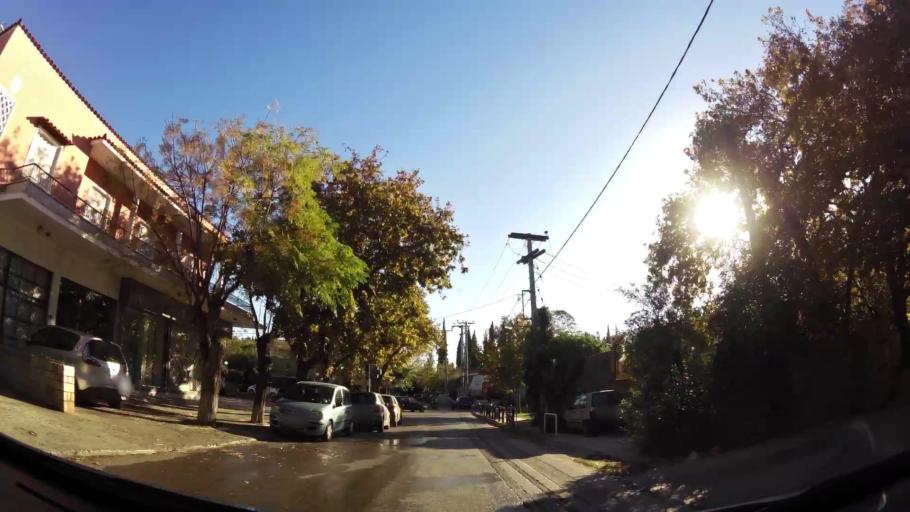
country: GR
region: Attica
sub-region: Nomarchia Athinas
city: Kifisia
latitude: 38.0781
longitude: 23.8044
